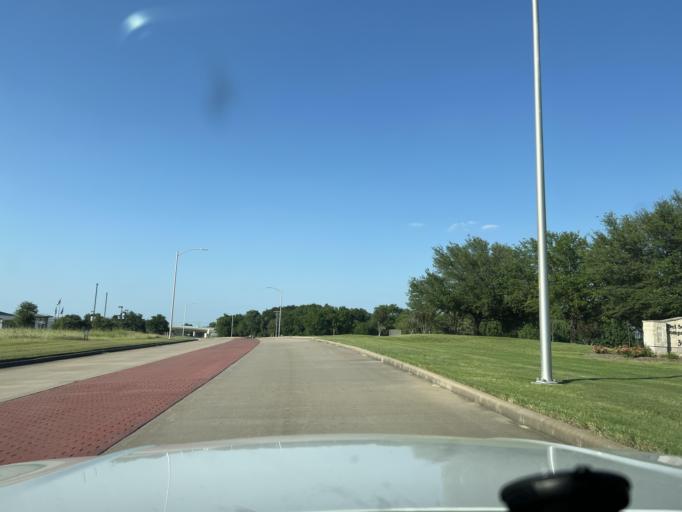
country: US
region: Texas
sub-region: Washington County
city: Brenham
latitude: 30.1402
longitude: -96.3657
